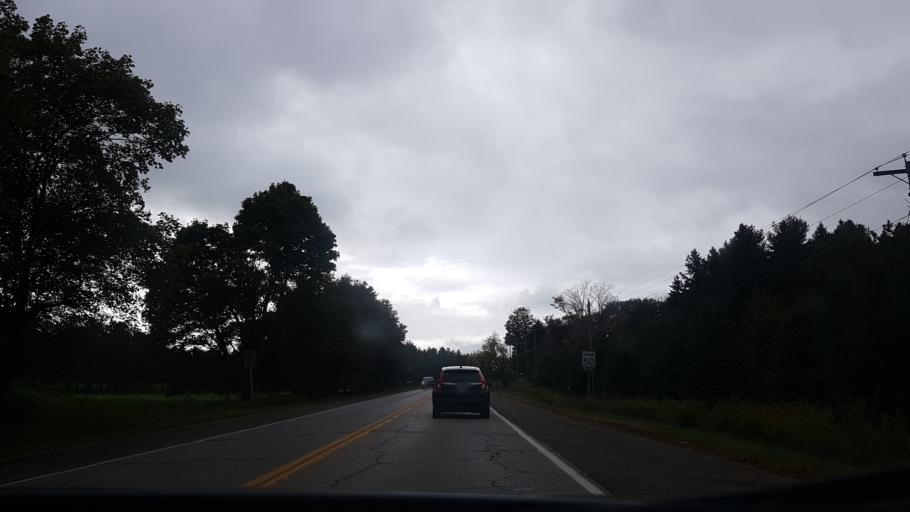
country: CA
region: Ontario
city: Uxbridge
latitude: 44.1037
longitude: -79.0952
